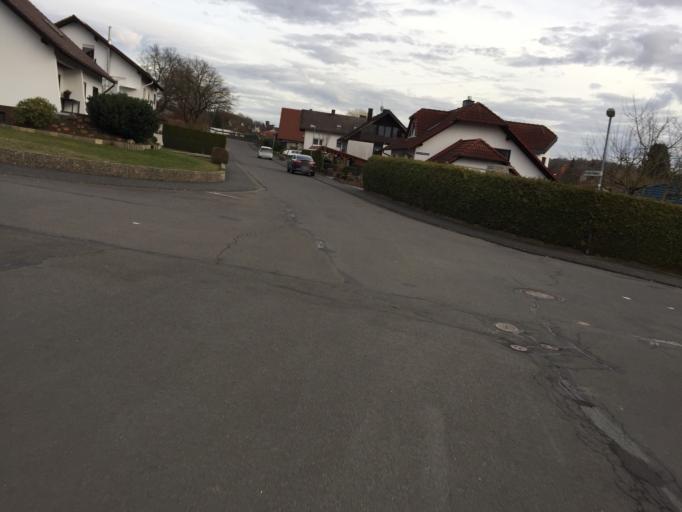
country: DE
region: Hesse
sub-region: Regierungsbezirk Giessen
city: Rabenau
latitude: 50.6727
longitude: 8.8706
